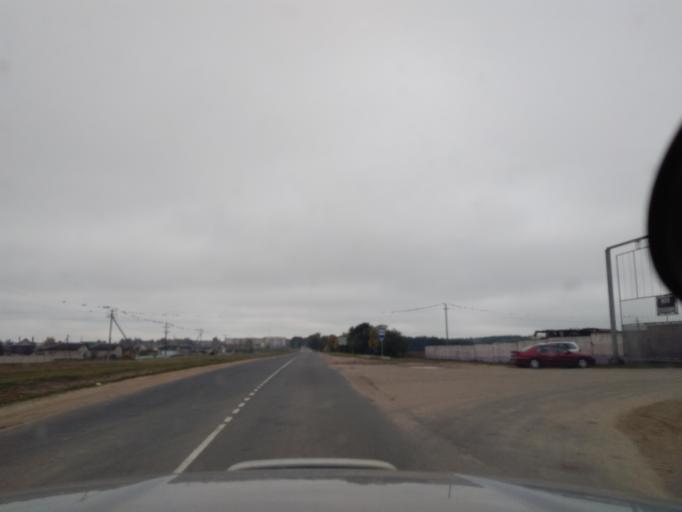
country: BY
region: Minsk
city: Kapyl'
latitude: 53.1501
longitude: 27.1325
